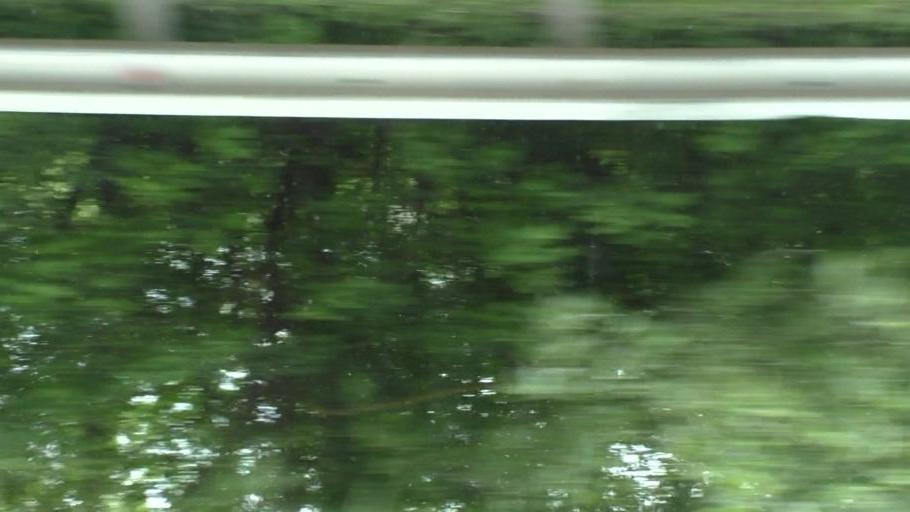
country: RU
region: Moskovskaya
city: Yegor'yevsk
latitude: 55.3954
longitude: 39.0166
